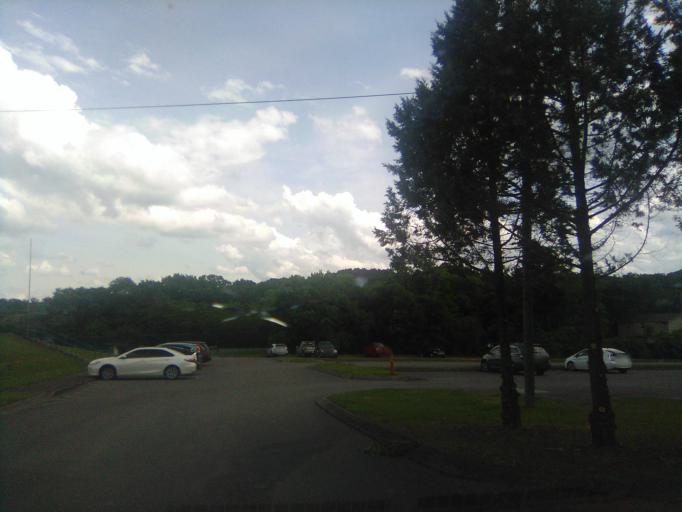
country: US
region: Tennessee
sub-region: Davidson County
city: Belle Meade
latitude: 36.0842
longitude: -86.8885
